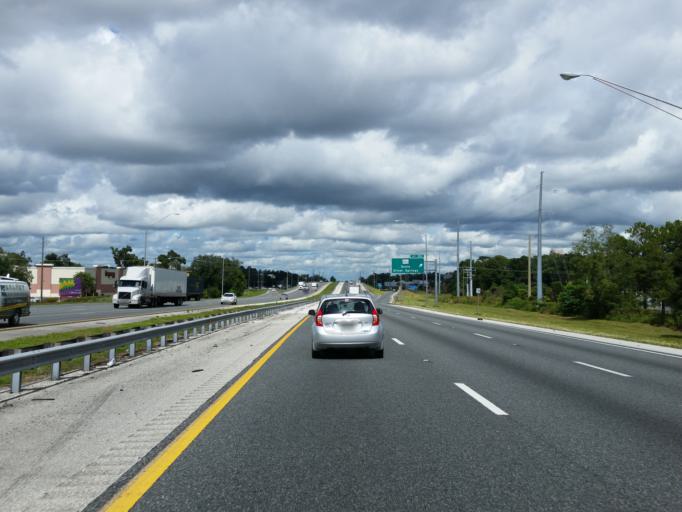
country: US
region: Florida
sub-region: Marion County
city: Ocala
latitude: 29.1440
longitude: -82.1850
